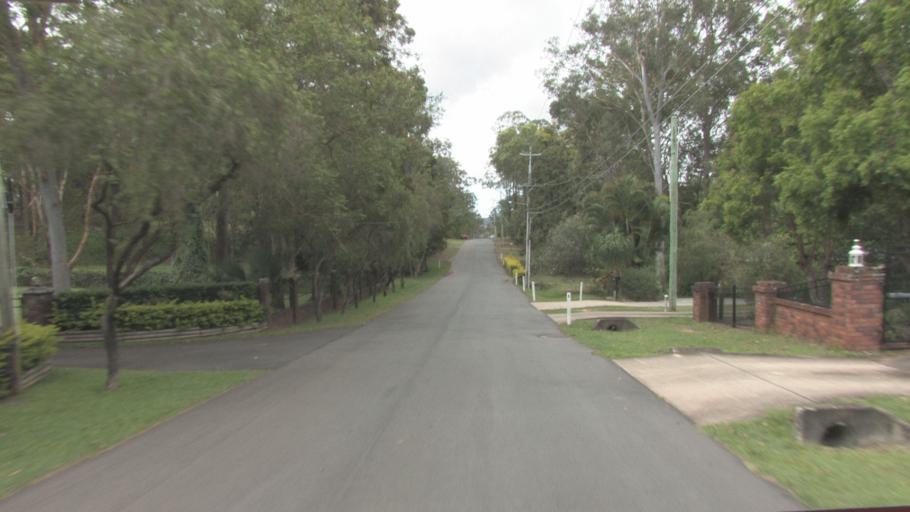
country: AU
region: Queensland
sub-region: Logan
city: Slacks Creek
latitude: -27.6693
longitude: 153.1713
